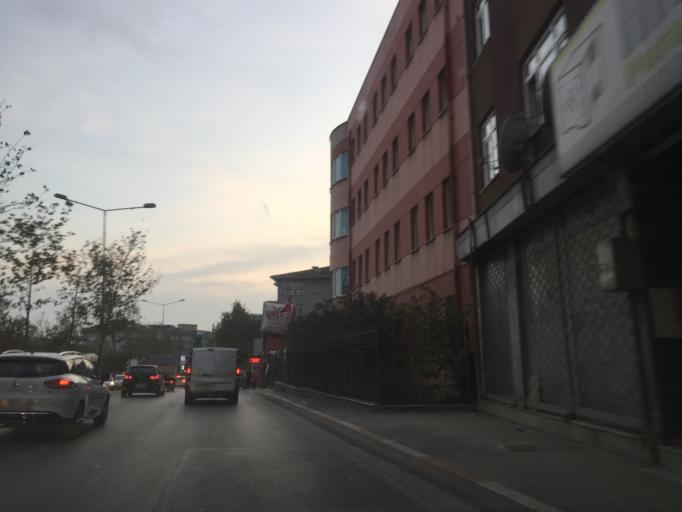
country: TR
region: Istanbul
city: Samandira
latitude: 40.9833
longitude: 29.2217
